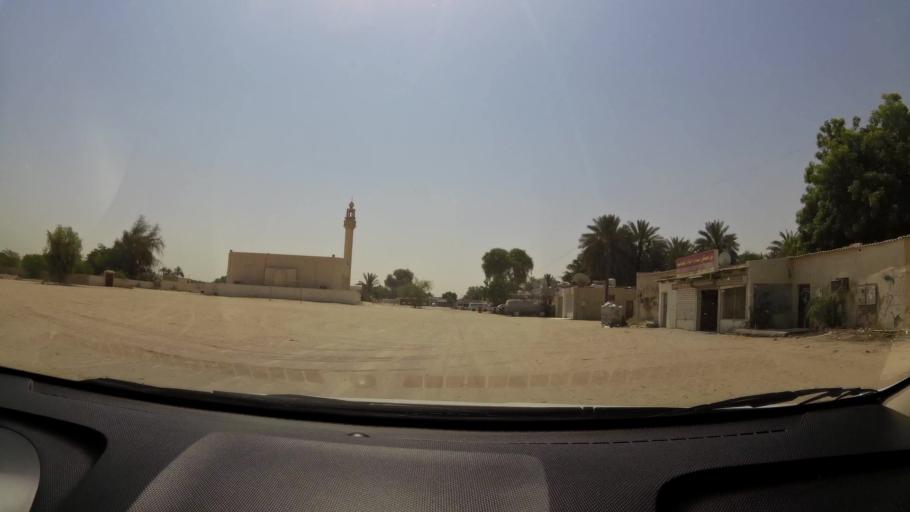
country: AE
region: Ajman
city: Ajman
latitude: 25.3961
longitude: 55.5282
